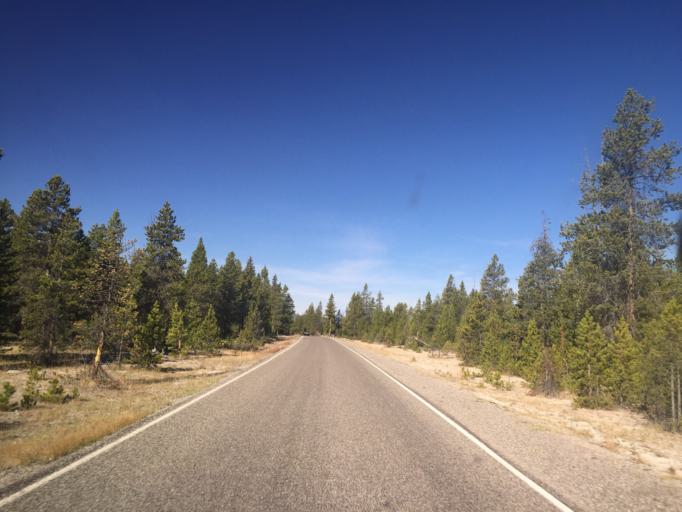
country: US
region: Montana
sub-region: Gallatin County
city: West Yellowstone
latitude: 44.5467
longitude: -110.7945
